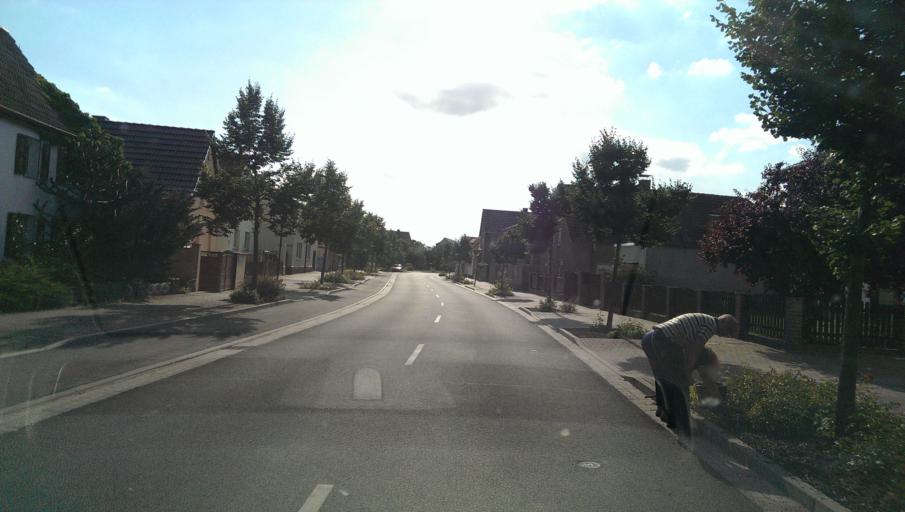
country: DE
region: Saxony
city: Lobnitz
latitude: 51.5922
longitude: 12.4605
